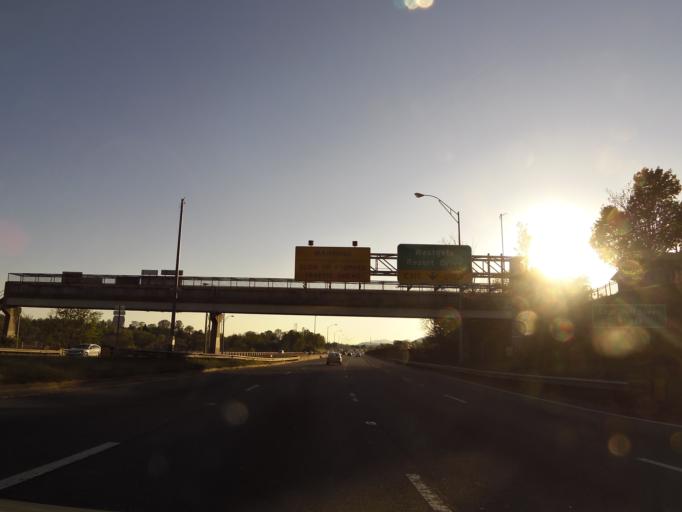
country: US
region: North Carolina
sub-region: Buncombe County
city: Asheville
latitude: 35.5915
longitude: -82.5693
